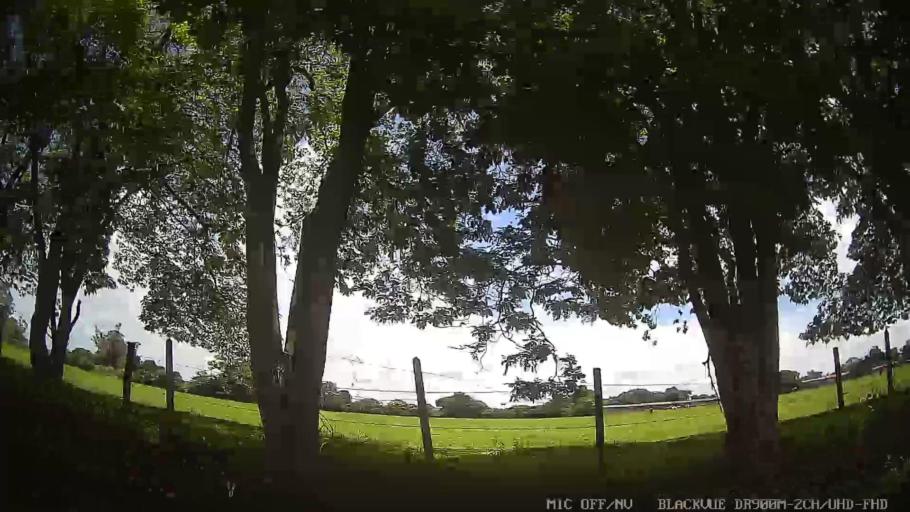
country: BR
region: Sao Paulo
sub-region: Laranjal Paulista
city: Laranjal Paulista
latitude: -23.0205
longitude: -47.8549
